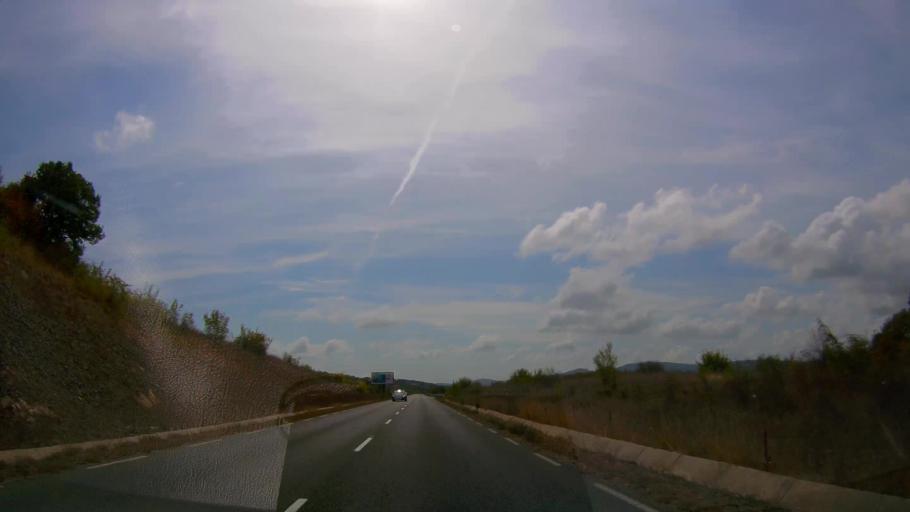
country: BG
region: Burgas
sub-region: Obshtina Sozopol
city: Sozopol
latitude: 42.3874
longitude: 27.6792
